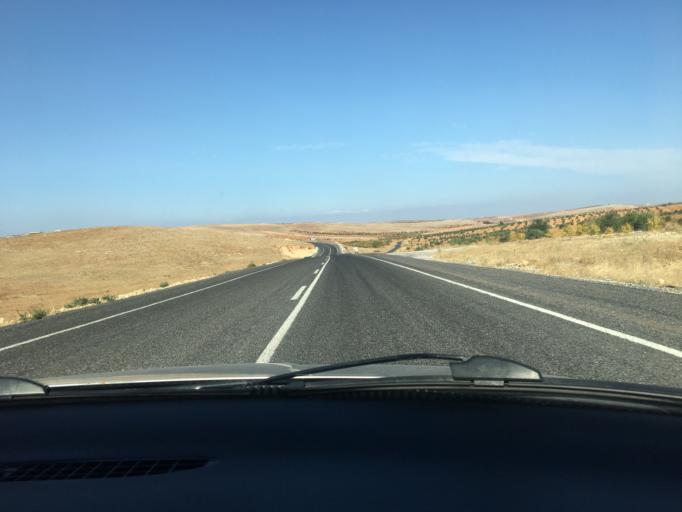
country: TR
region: Sanliurfa
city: Bogurtlen
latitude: 37.1627
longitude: 37.9813
